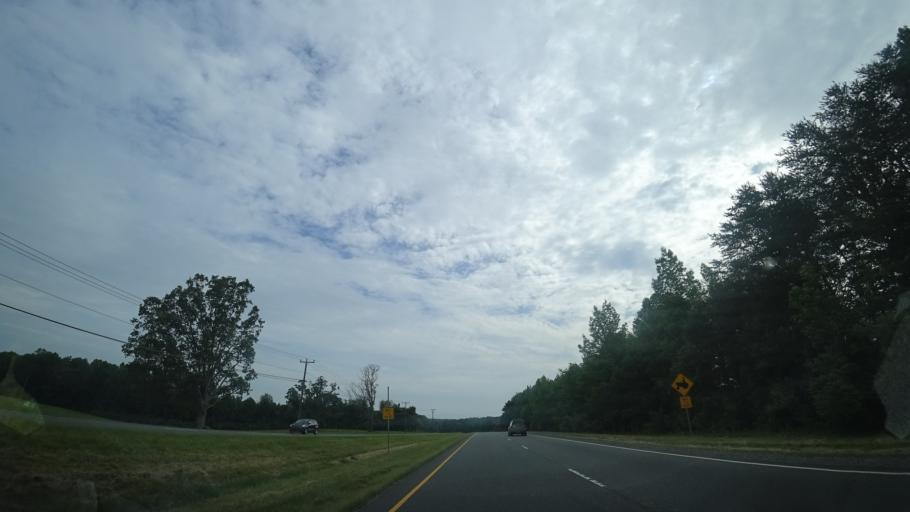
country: US
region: Virginia
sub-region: Spotsylvania County
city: Spotsylvania
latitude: 38.2114
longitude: -77.5752
